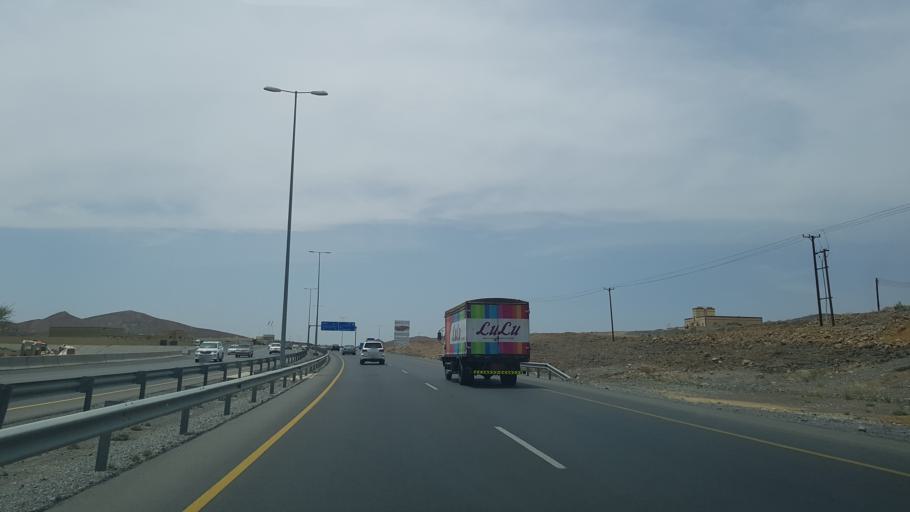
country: OM
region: Muhafazat ad Dakhiliyah
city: Izki
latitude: 22.9099
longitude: 57.7504
